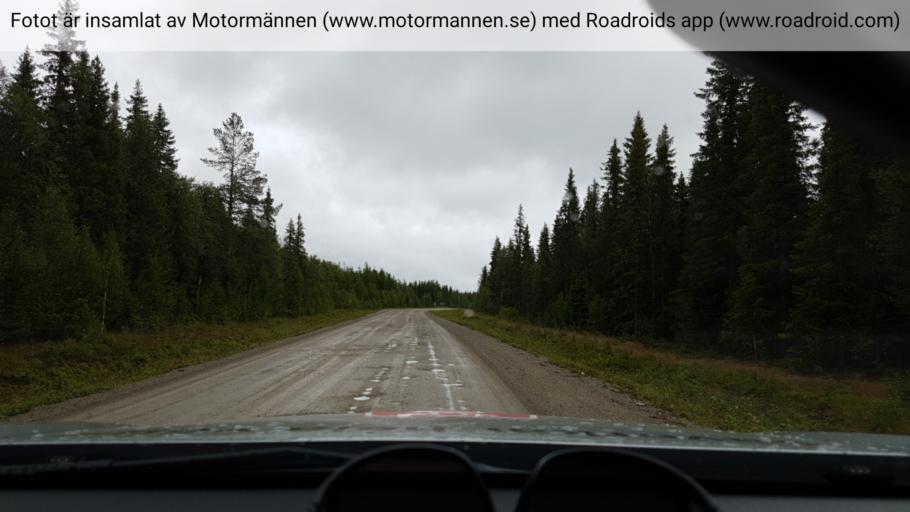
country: SE
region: Vaesterbotten
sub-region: Storumans Kommun
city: Storuman
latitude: 64.8513
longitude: 17.4089
